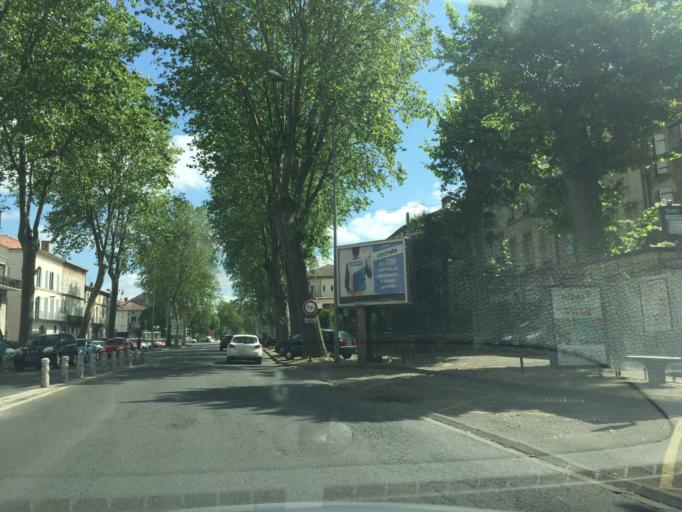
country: FR
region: Aquitaine
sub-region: Departement du Lot-et-Garonne
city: Le Passage
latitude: 44.2058
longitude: 0.6116
